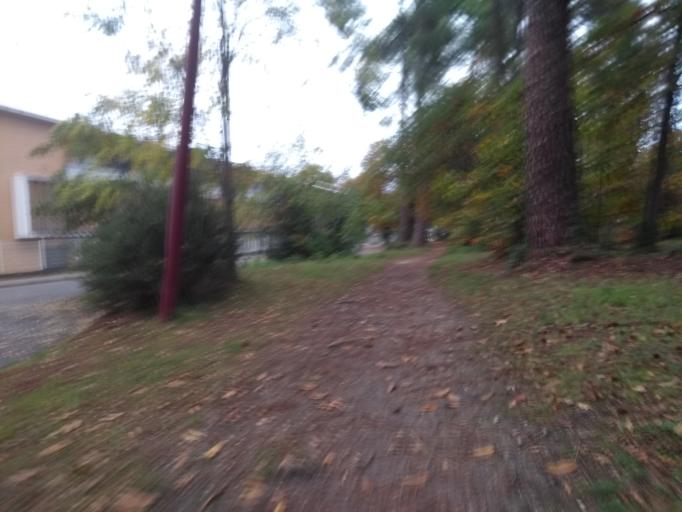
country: FR
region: Aquitaine
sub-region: Departement de la Gironde
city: Gradignan
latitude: 44.7759
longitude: -0.6068
